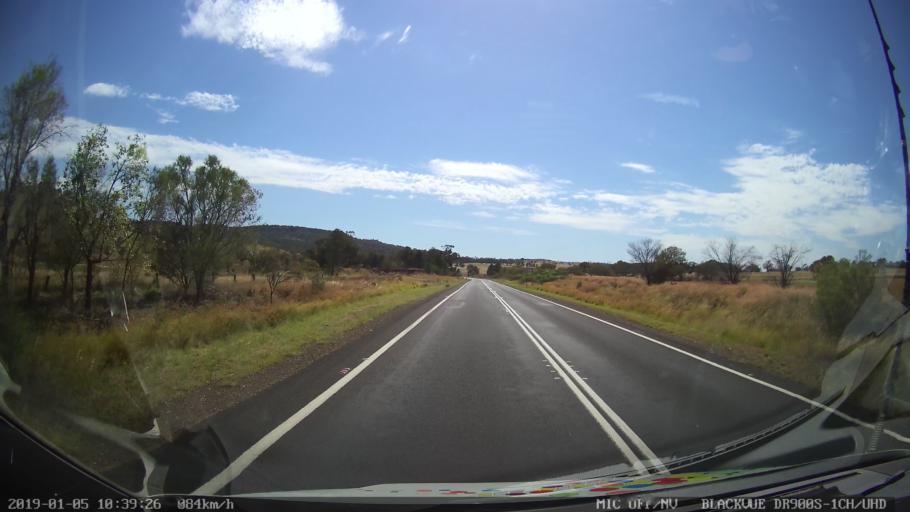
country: AU
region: New South Wales
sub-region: Gilgandra
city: Gilgandra
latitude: -31.4681
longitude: 148.9299
